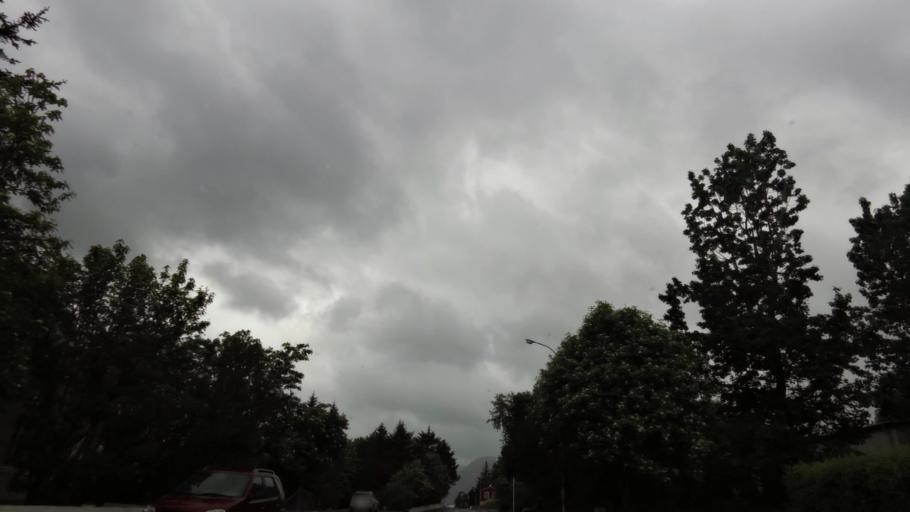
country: IS
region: Westfjords
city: Isafjoerdur
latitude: 65.8789
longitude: -23.4981
